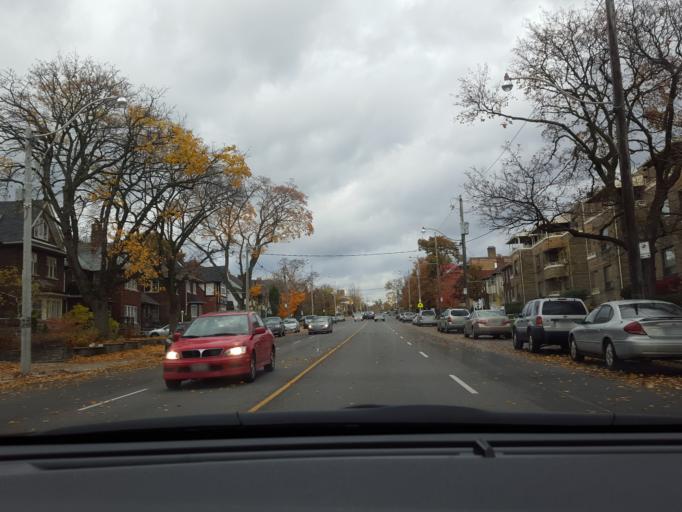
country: CA
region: Ontario
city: Toronto
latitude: 43.6999
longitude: -79.4066
